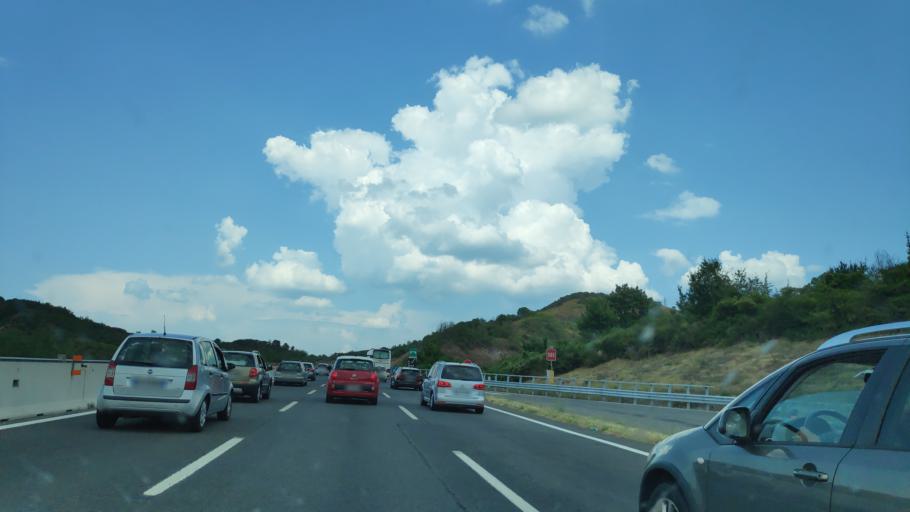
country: IT
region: Umbria
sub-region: Provincia di Terni
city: Ficulle
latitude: 42.8304
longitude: 12.0427
